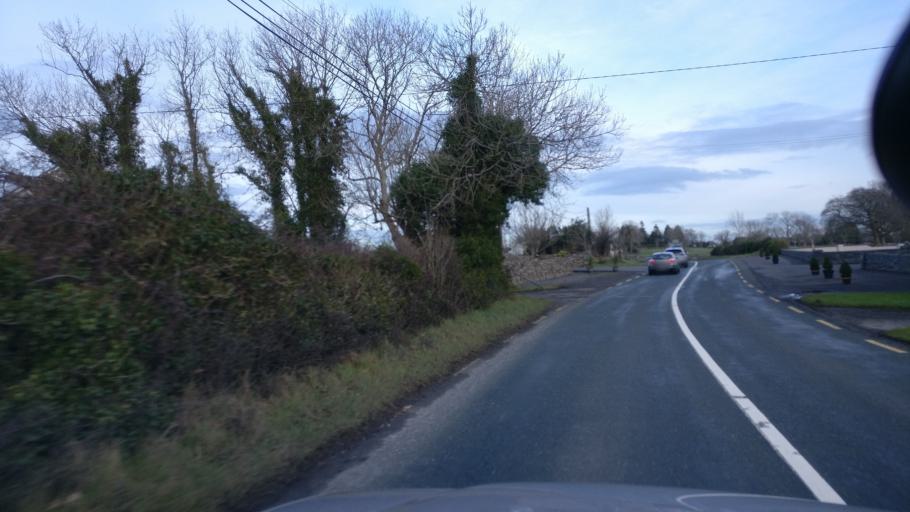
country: IE
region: Connaught
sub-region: Maigh Eo
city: Ballinrobe
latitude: 53.5399
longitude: -9.2368
